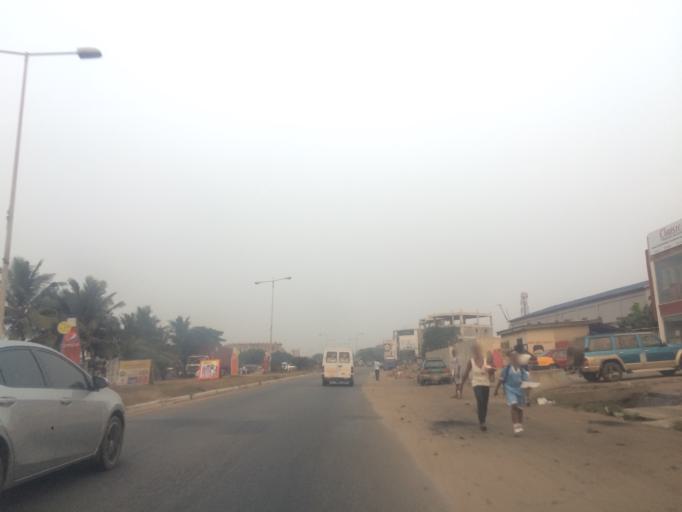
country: GH
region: Greater Accra
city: Accra
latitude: 5.5576
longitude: -0.1571
